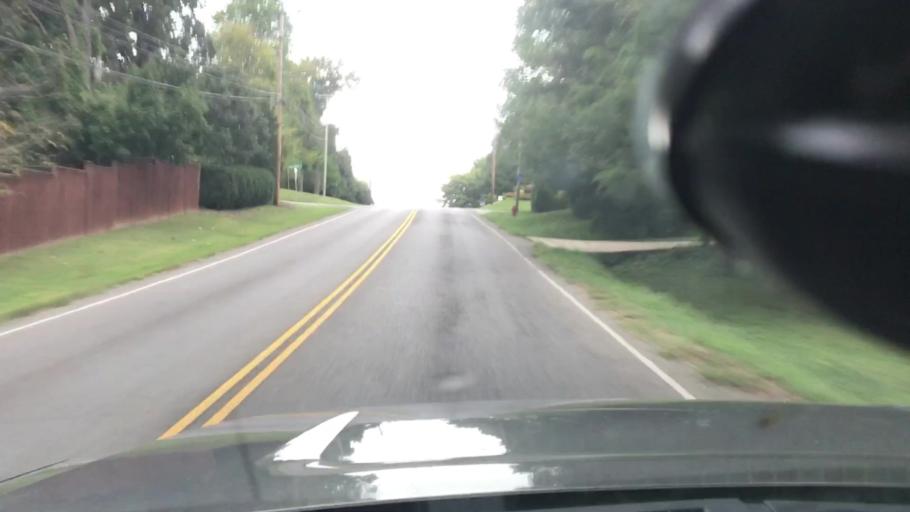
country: US
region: Tennessee
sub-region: Davidson County
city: Oak Hill
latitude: 36.1100
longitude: -86.7786
